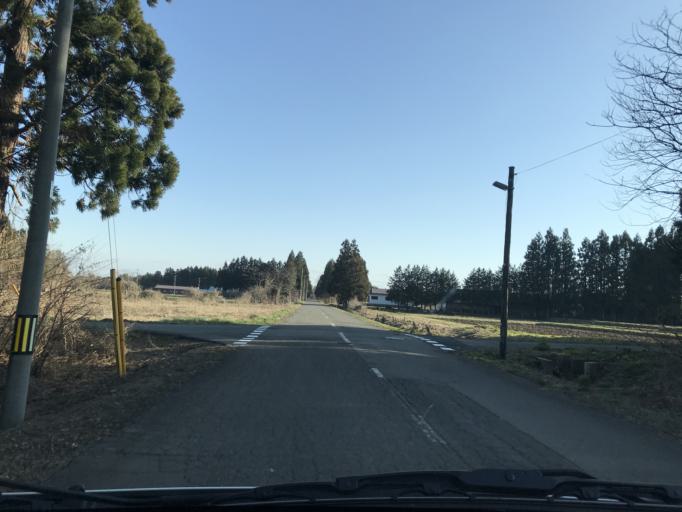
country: JP
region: Iwate
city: Kitakami
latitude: 39.2472
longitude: 141.0399
